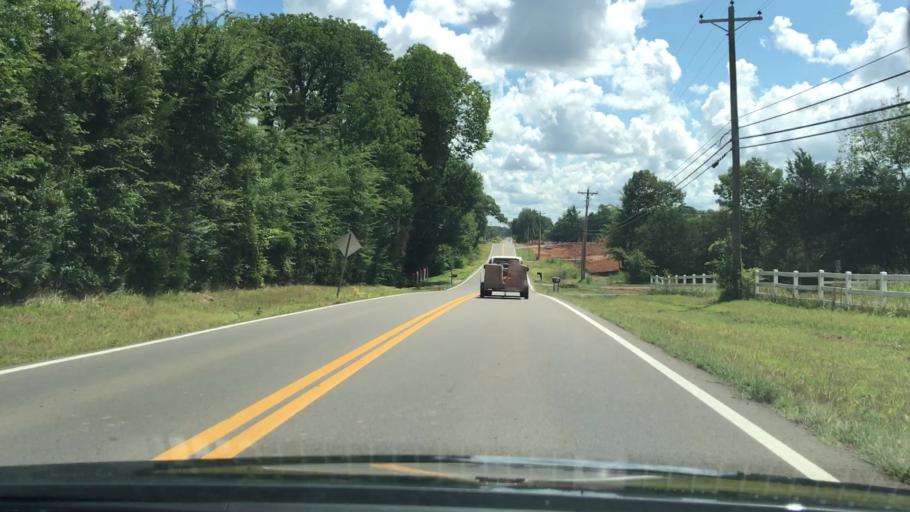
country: US
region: Tennessee
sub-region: Rutherford County
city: Smyrna
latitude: 35.8433
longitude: -86.5405
